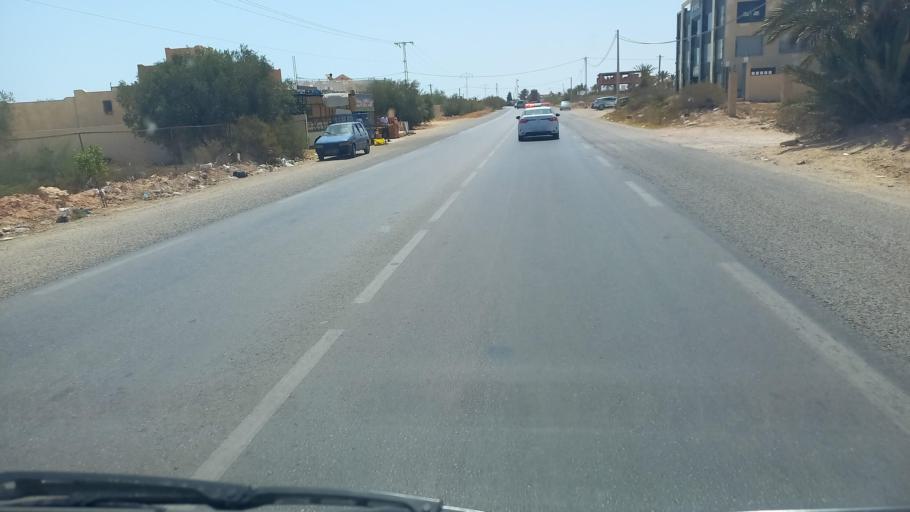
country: TN
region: Madanin
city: Houmt Souk
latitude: 33.8135
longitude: 10.8764
